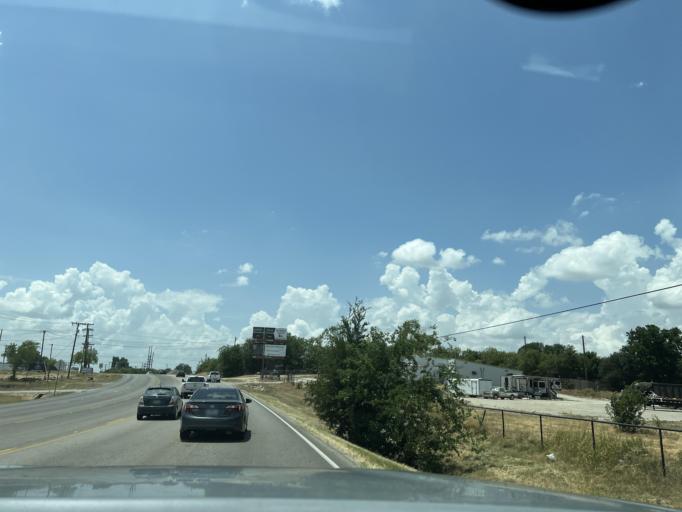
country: US
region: Texas
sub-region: Parker County
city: Weatherford
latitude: 32.7840
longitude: -97.7970
